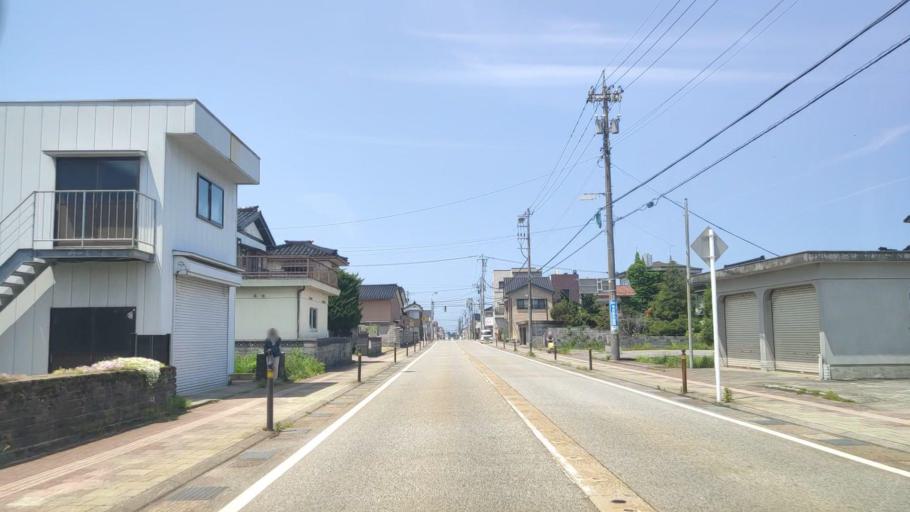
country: JP
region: Toyama
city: Nyuzen
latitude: 36.9537
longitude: 137.5614
